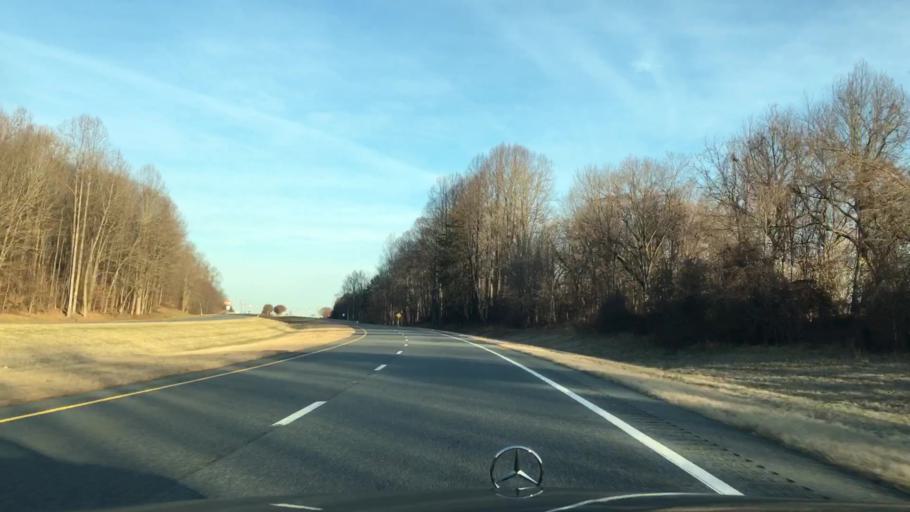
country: US
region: North Carolina
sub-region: Guilford County
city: Greensboro
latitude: 36.0235
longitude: -79.7650
